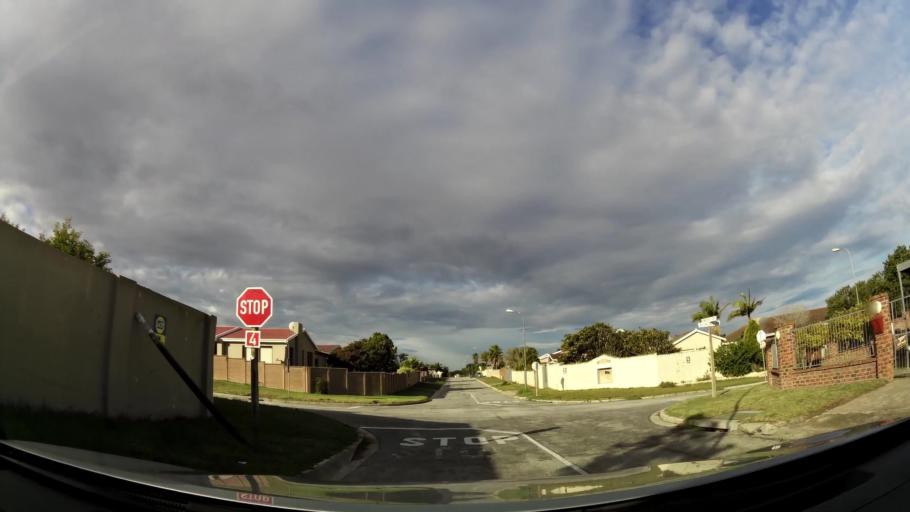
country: ZA
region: Eastern Cape
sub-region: Nelson Mandela Bay Metropolitan Municipality
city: Port Elizabeth
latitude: -33.9463
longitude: 25.4854
